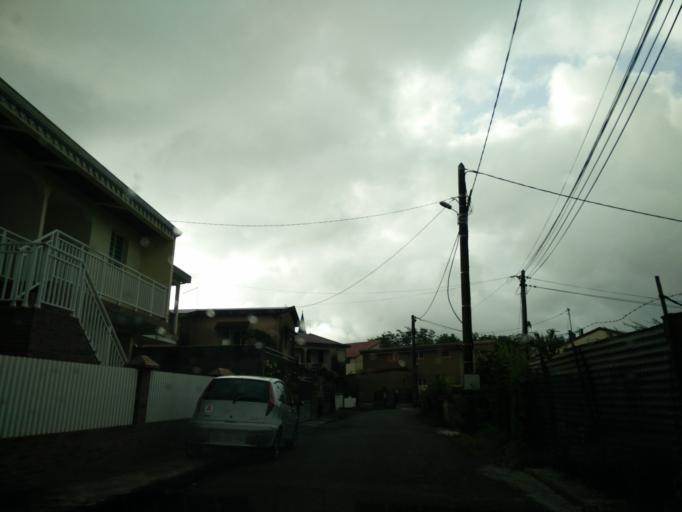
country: MQ
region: Martinique
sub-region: Martinique
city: Le Morne-Rouge
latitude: 14.7736
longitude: -61.1338
